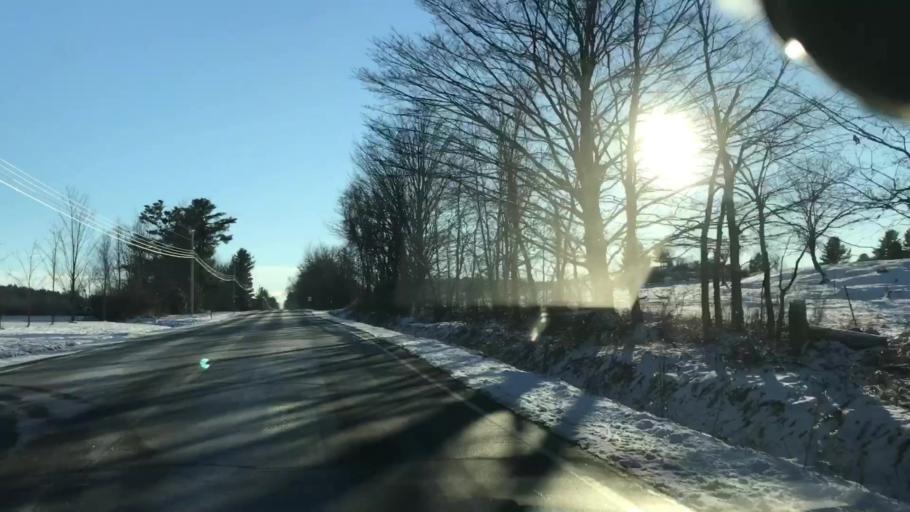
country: US
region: New Hampshire
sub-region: Grafton County
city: Haverhill
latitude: 44.0000
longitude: -72.0743
